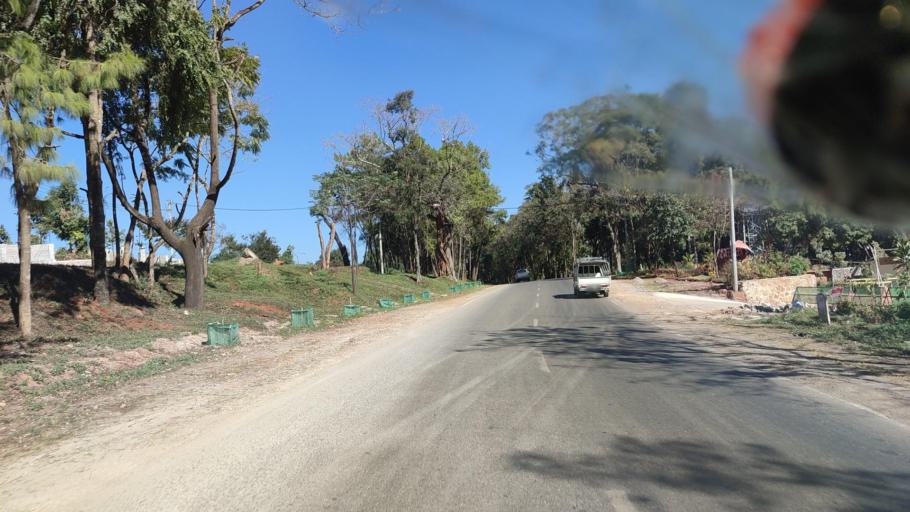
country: MM
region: Mandalay
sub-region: Pyin Oo Lwin District
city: Pyin Oo Lwin
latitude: 21.9985
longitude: 96.4304
